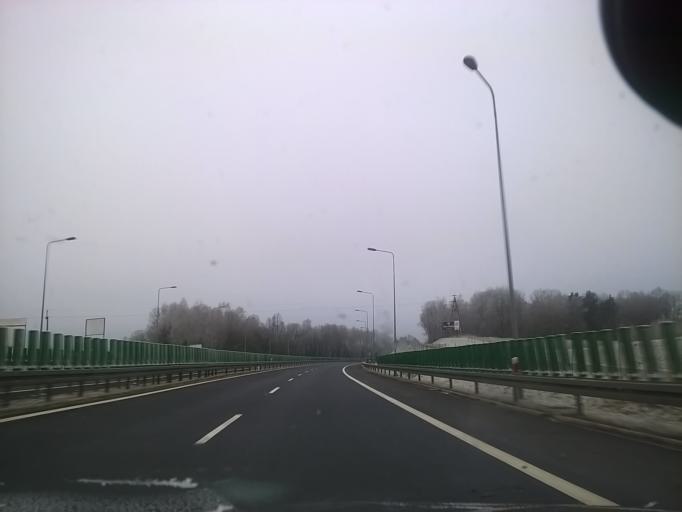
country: PL
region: Warmian-Masurian Voivodeship
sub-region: Powiat olsztynski
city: Barczewo
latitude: 53.8264
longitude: 20.8110
